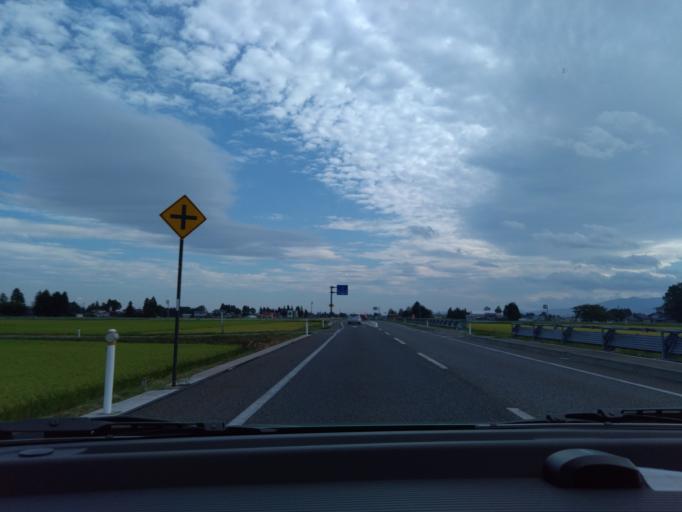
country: JP
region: Iwate
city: Hanamaki
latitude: 39.3711
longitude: 141.0567
